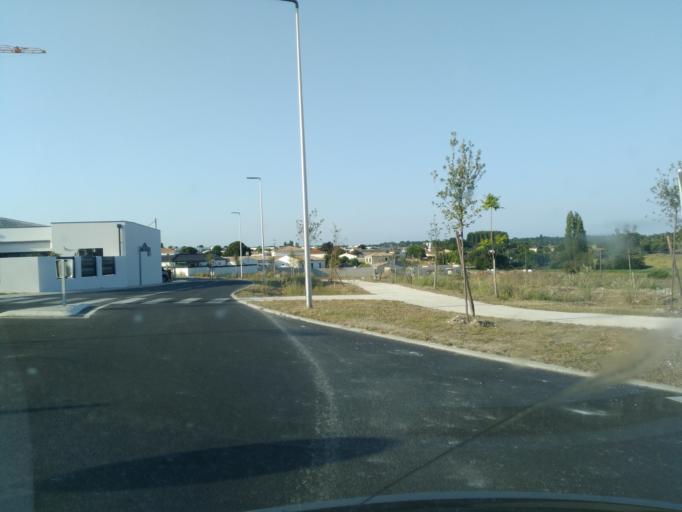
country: FR
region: Poitou-Charentes
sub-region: Departement de la Charente-Maritime
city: Vaux-sur-Mer
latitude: 45.6403
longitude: -1.0537
